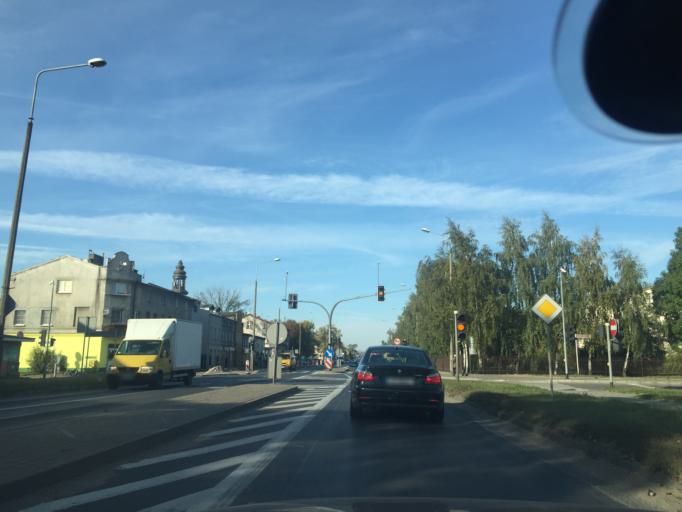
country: PL
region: Kujawsko-Pomorskie
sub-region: Powiat inowroclawski
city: Inowroclaw
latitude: 52.7531
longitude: 18.2561
